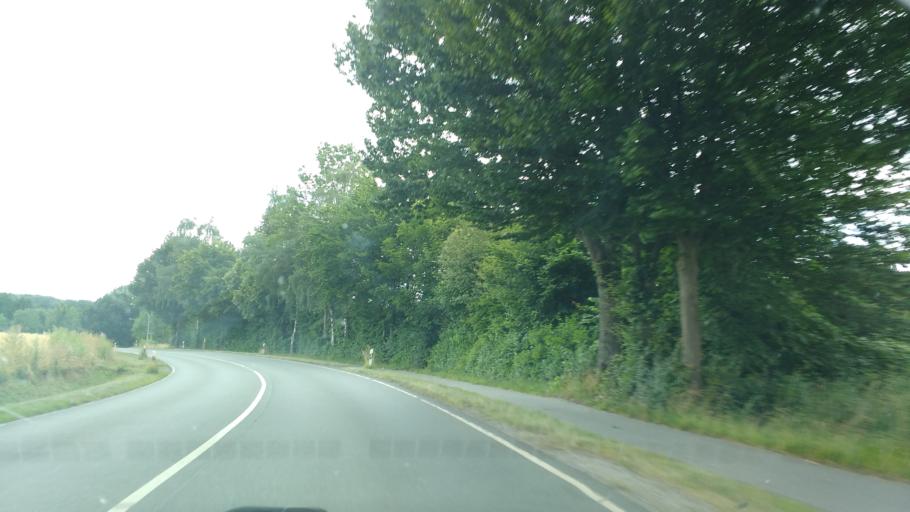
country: DE
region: North Rhine-Westphalia
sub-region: Regierungsbezirk Detmold
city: Horn-Bad Meinberg
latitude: 51.8956
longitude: 8.9664
